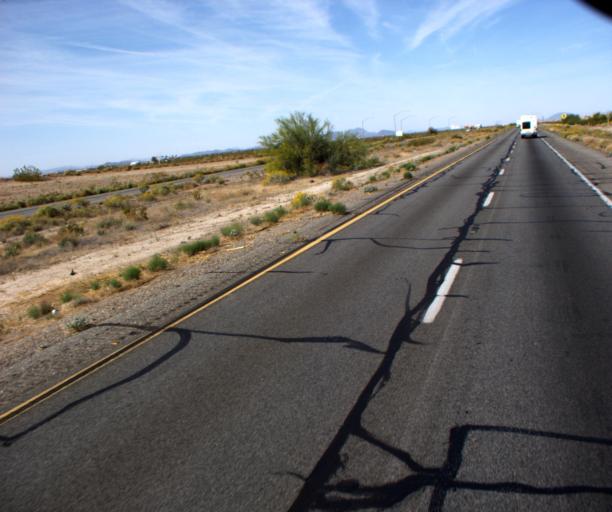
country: US
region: Arizona
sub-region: Maricopa County
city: Buckeye
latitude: 33.4396
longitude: -112.6784
